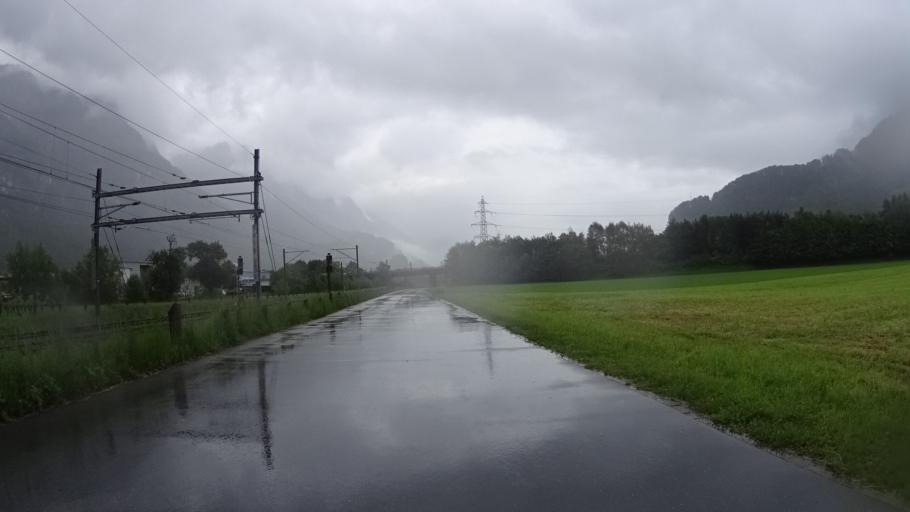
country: CH
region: Saint Gallen
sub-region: Wahlkreis Sarganserland
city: Walenstadt
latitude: 47.1168
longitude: 9.3211
